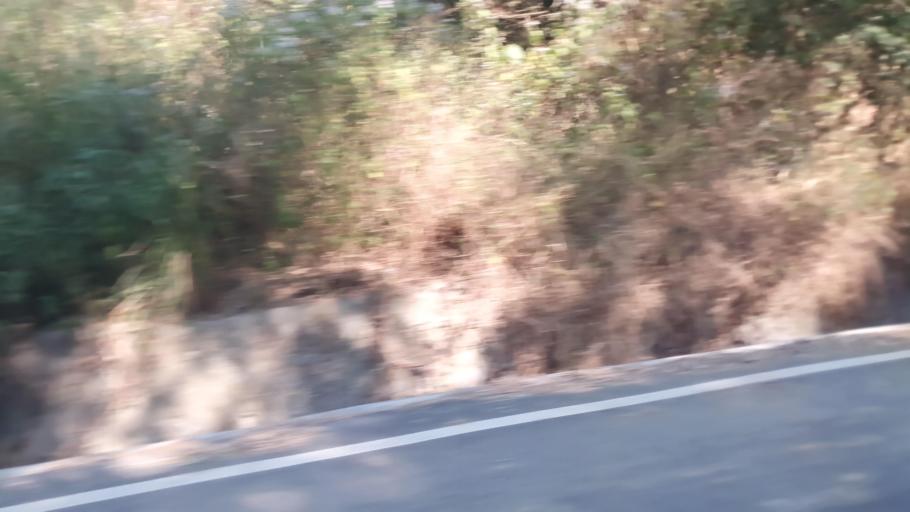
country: TW
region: Taiwan
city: Yujing
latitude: 23.0408
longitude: 120.3978
